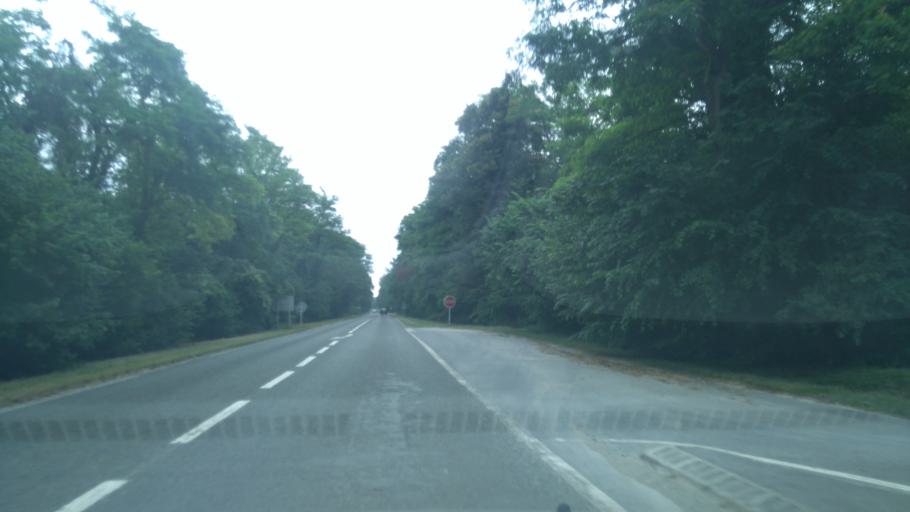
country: FR
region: Picardie
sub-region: Departement de l'Oise
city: Saint-Maximin
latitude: 49.2102
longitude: 2.4469
